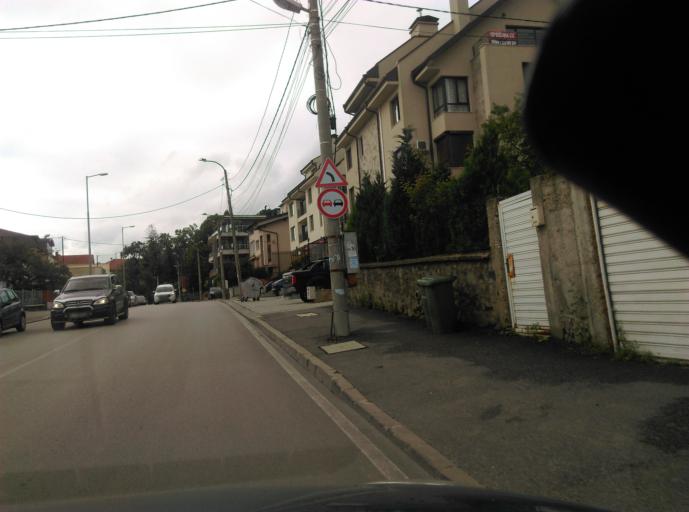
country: BG
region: Sofia-Capital
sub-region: Stolichna Obshtina
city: Sofia
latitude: 42.6301
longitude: 23.3070
